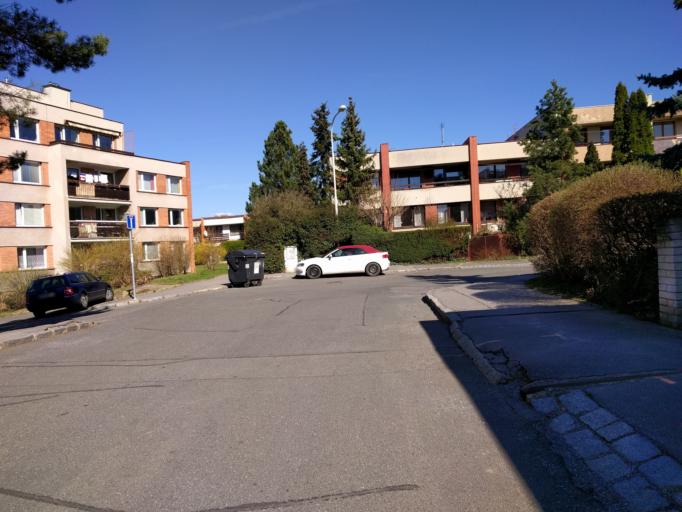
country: CZ
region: Praha
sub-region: Praha 1
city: Mala Strana
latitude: 50.1147
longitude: 14.3821
